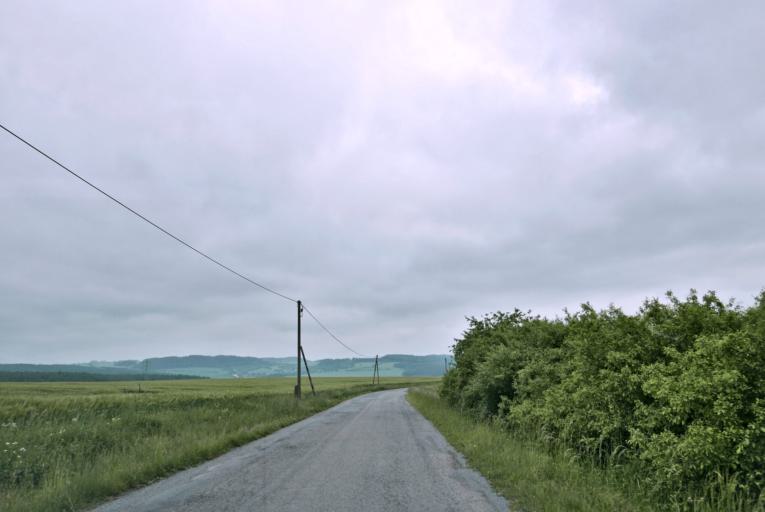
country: CZ
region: Plzensky
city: Zihle
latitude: 49.9927
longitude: 13.3469
